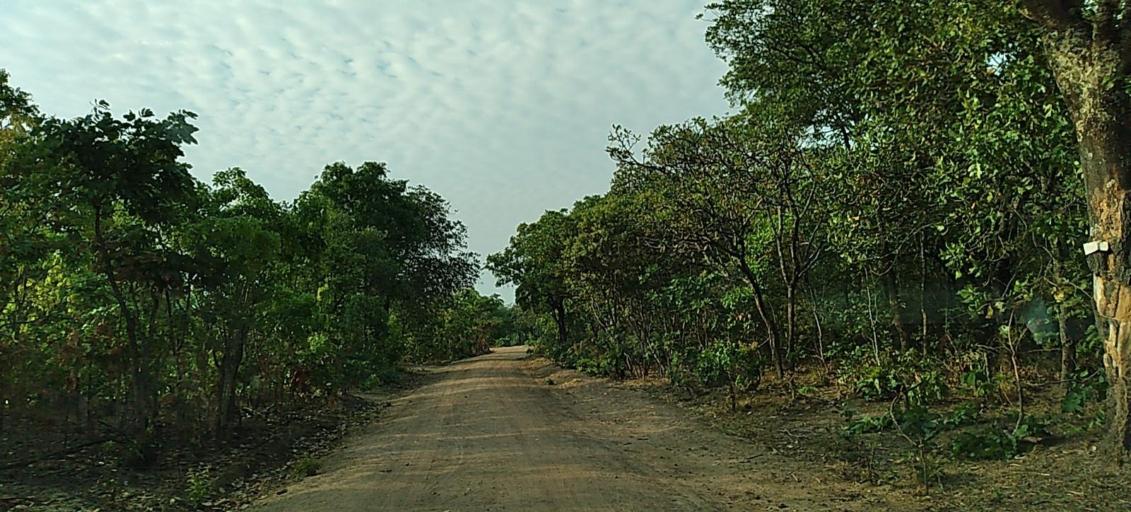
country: ZM
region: Copperbelt
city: Chingola
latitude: -12.8672
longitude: 27.6867
